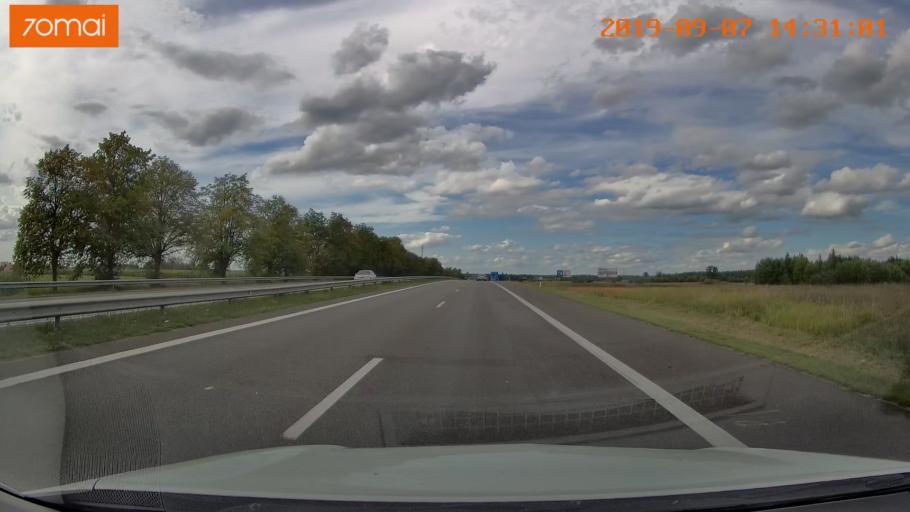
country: LT
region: Kauno apskritis
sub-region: Kauno rajonas
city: Karmelava
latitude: 54.8721
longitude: 24.2336
